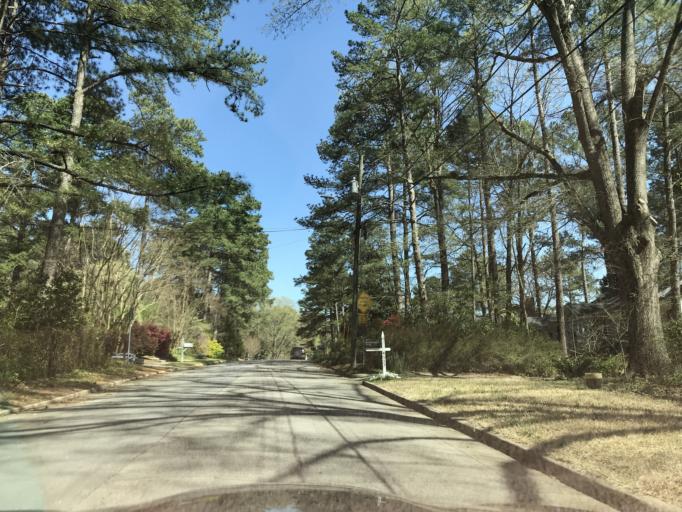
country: US
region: North Carolina
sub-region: Wake County
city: West Raleigh
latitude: 35.7721
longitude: -78.7051
